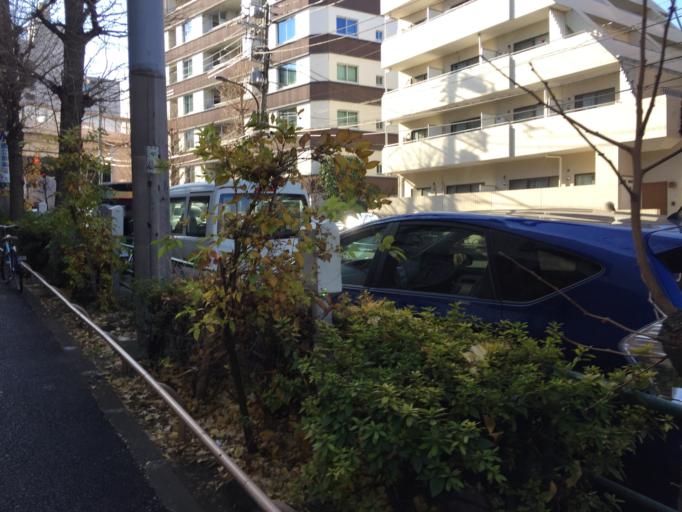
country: JP
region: Tokyo
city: Tokyo
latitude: 35.6479
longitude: 139.6777
